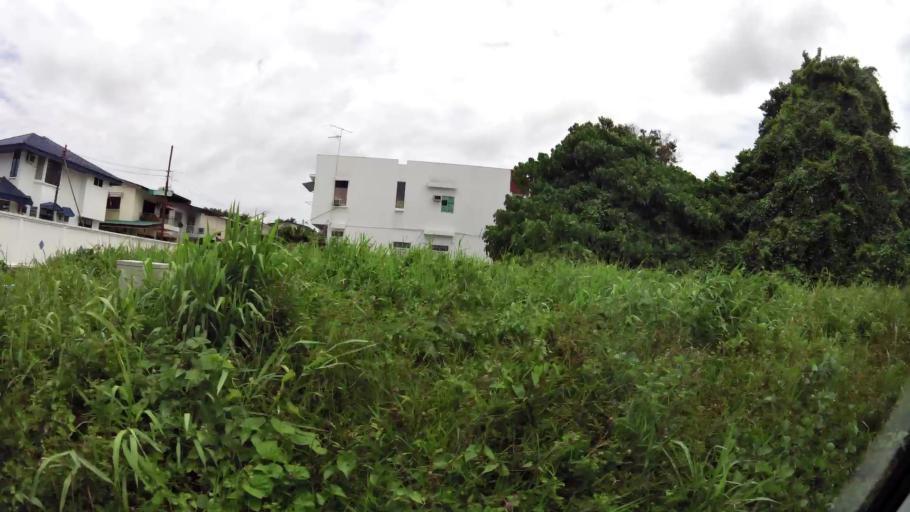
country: BN
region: Brunei and Muara
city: Bandar Seri Begawan
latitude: 4.9134
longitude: 114.9211
